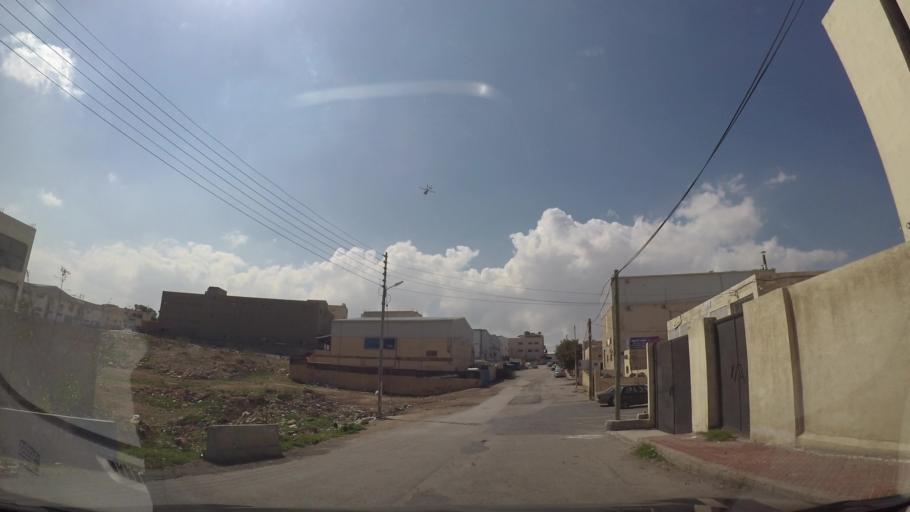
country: JO
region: Zarqa
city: Russeifa
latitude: 31.9879
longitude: 36.0158
